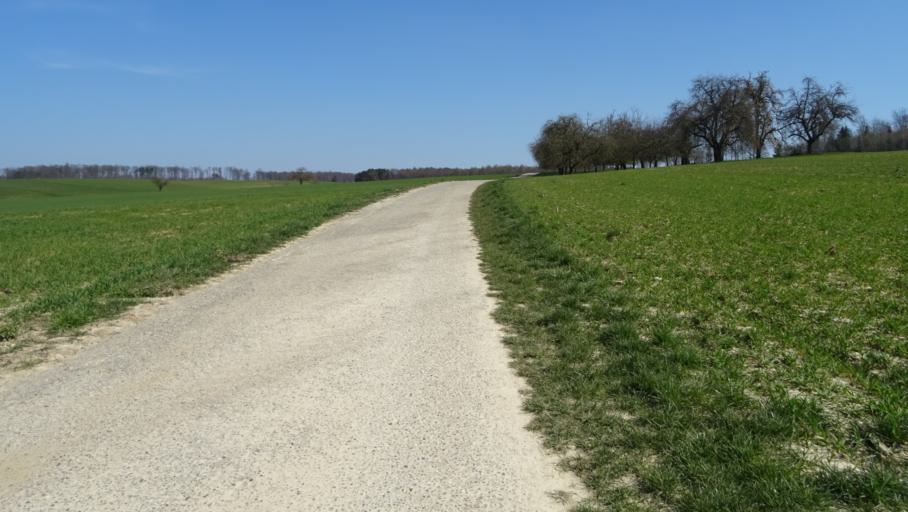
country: DE
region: Baden-Wuerttemberg
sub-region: Karlsruhe Region
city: Seckach
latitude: 49.4029
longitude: 9.3018
